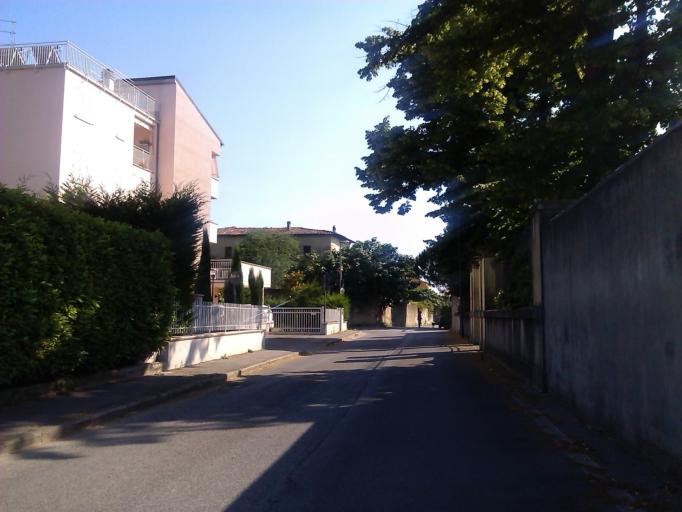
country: IT
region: Tuscany
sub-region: Province of Florence
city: Campi Bisenzio
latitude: 43.8410
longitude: 11.1324
